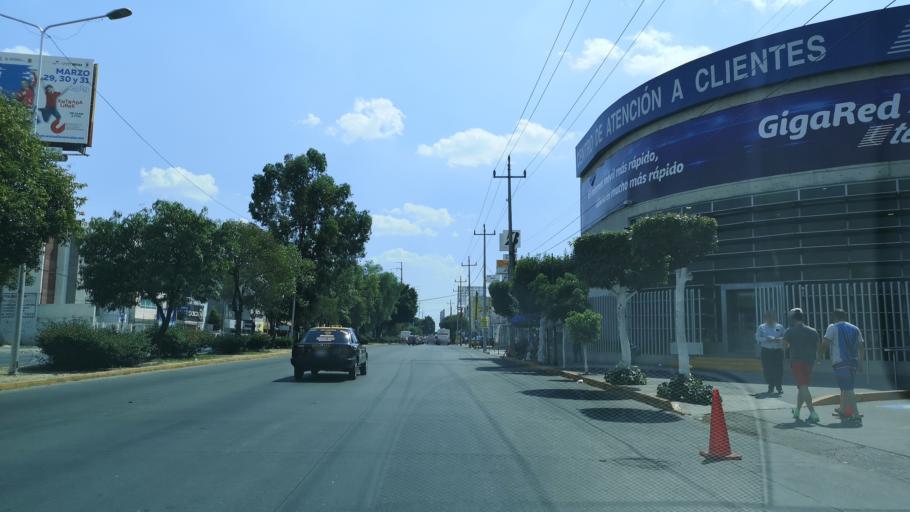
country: MX
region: Puebla
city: Puebla
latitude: 19.0640
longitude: -98.2153
